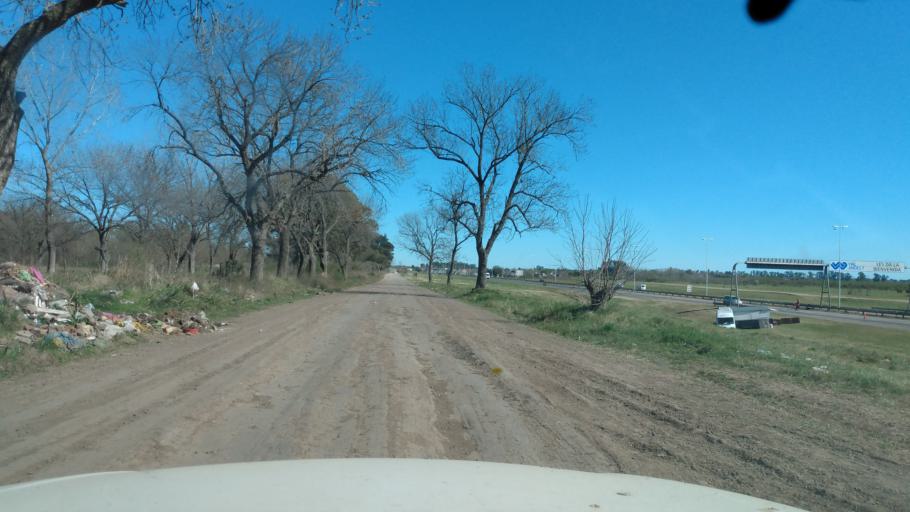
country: AR
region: Buenos Aires
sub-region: Partido de Lujan
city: Lujan
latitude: -34.5670
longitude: -59.0707
